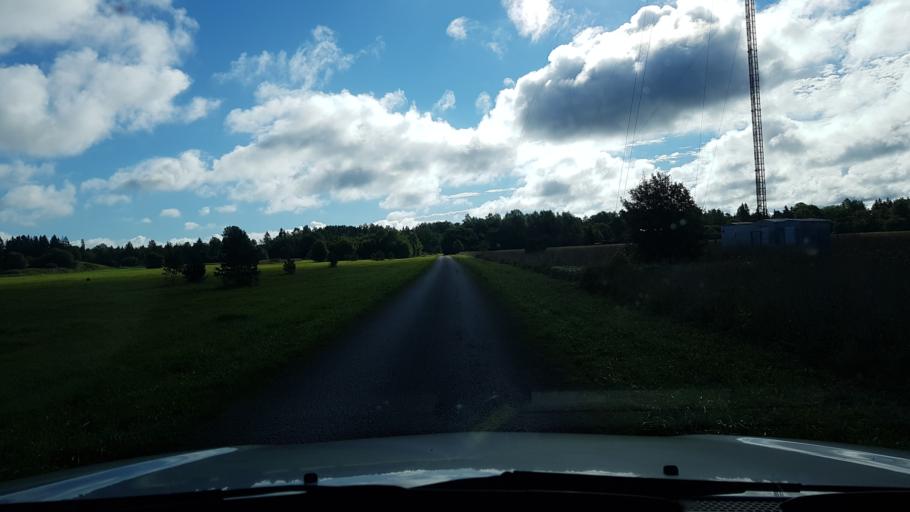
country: EE
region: Harju
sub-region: Rae vald
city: Vaida
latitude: 59.2519
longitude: 25.0192
